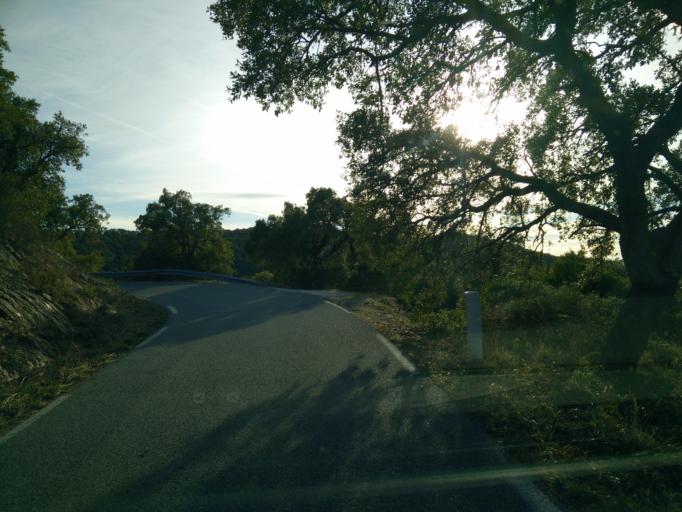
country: FR
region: Provence-Alpes-Cote d'Azur
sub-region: Departement du Var
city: Collobrieres
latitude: 43.1896
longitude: 6.3172
